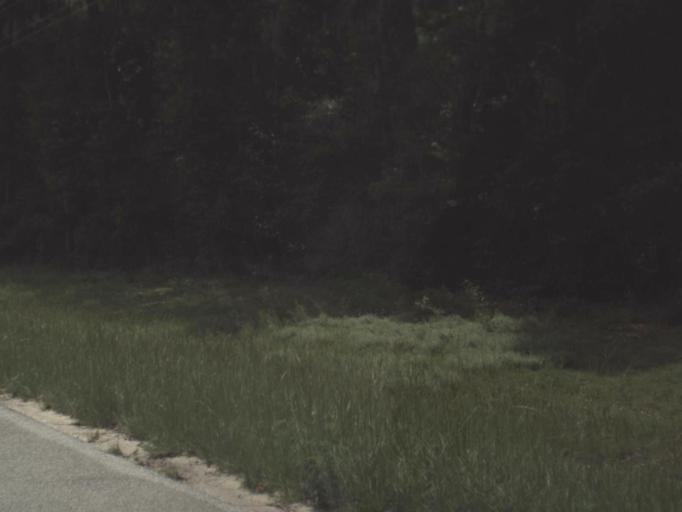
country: US
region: Florida
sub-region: Madison County
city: Madison
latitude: 30.4704
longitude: -83.3695
